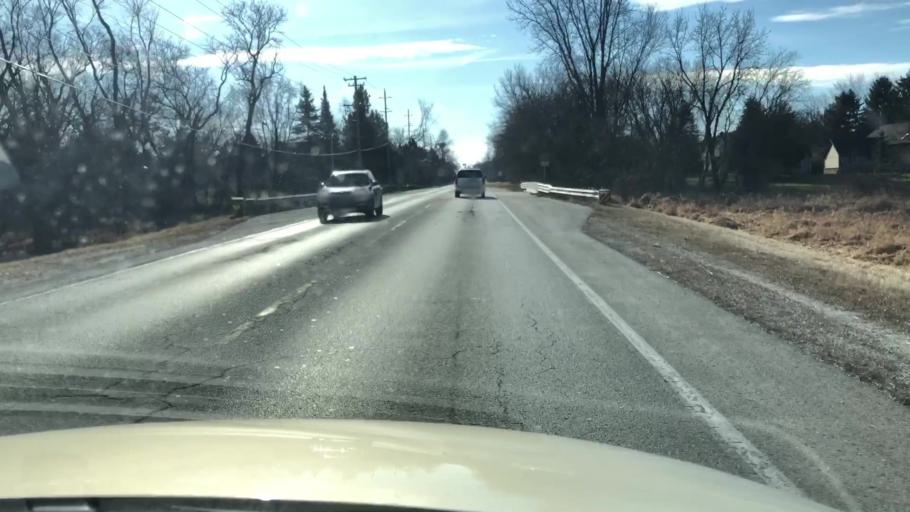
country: US
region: Wisconsin
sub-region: Waukesha County
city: Brookfield
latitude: 43.0449
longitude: -88.1666
